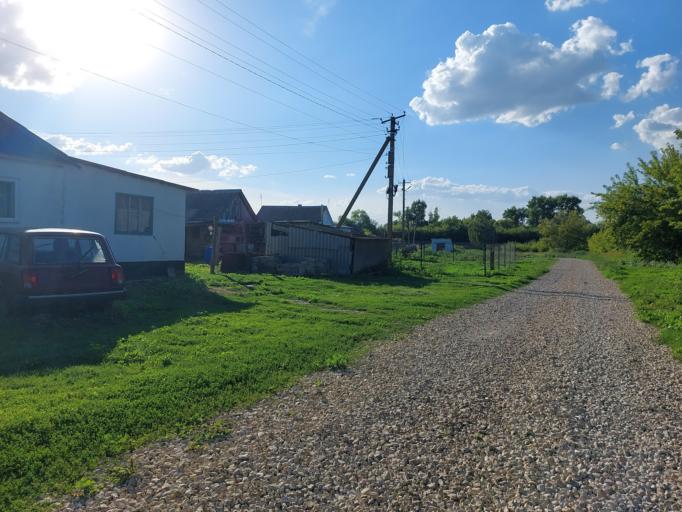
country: RU
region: Lipetsk
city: Terbuny
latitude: 52.2756
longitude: 38.1952
